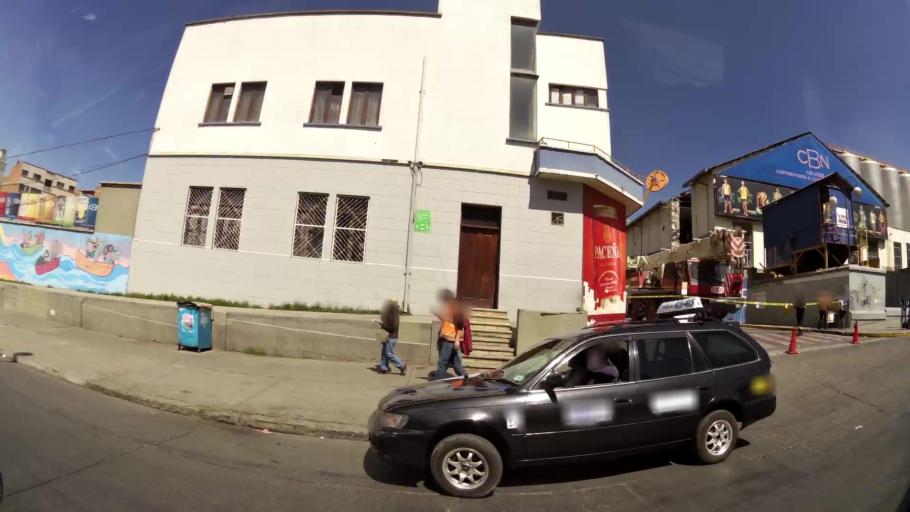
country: BO
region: La Paz
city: La Paz
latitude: -16.4900
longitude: -68.1421
